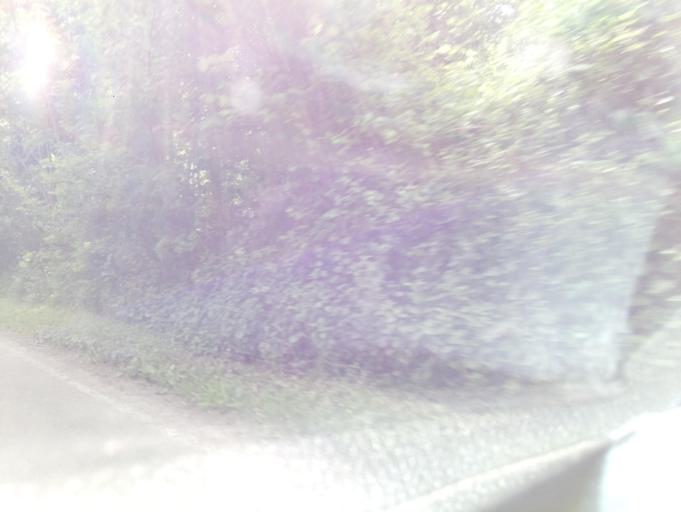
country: GB
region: England
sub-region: Herefordshire
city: Yatton
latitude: 51.9620
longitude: -2.5275
